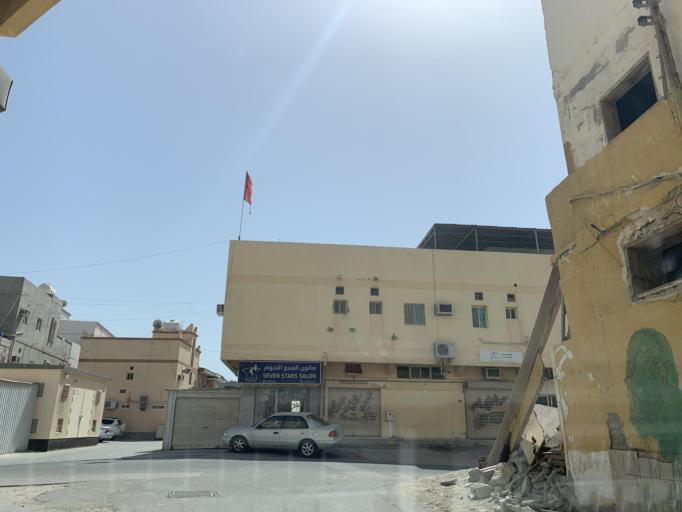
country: BH
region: Northern
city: Sitrah
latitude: 26.1459
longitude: 50.6087
